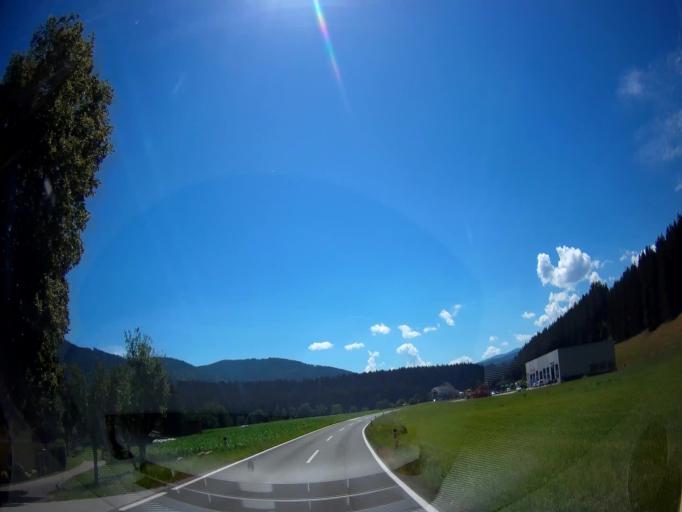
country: AT
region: Carinthia
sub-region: Politischer Bezirk Sankt Veit an der Glan
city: Glodnitz
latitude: 46.8519
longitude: 14.1575
